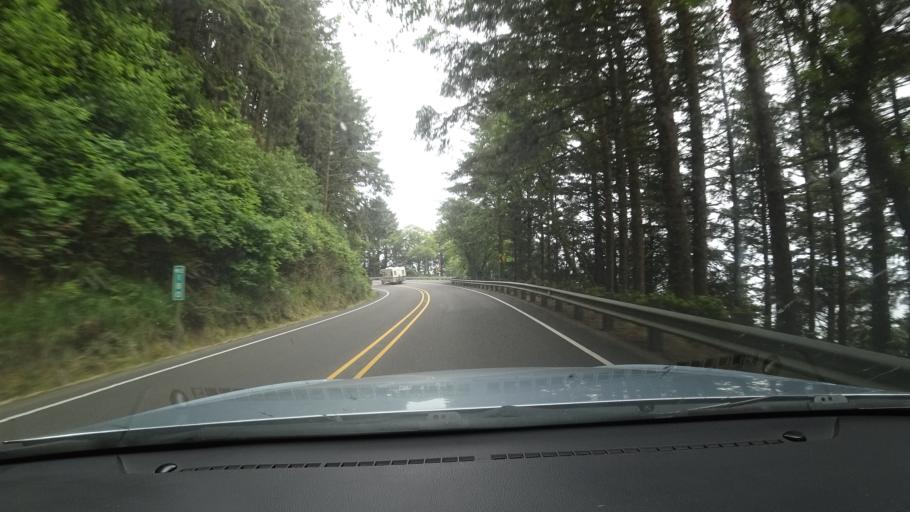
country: US
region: Oregon
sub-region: Lane County
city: Florence
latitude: 44.1165
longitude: -124.1218
